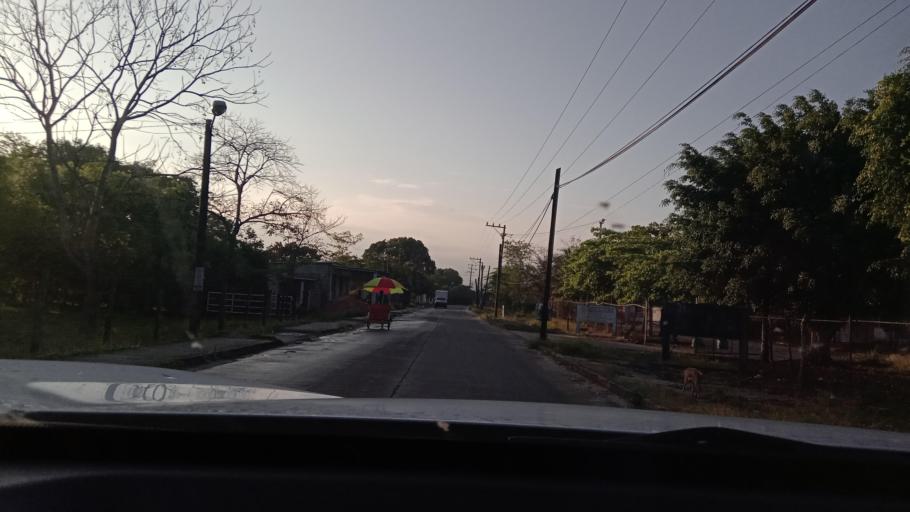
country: MX
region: Veracruz
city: Las Choapas
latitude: 17.8859
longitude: -94.0989
